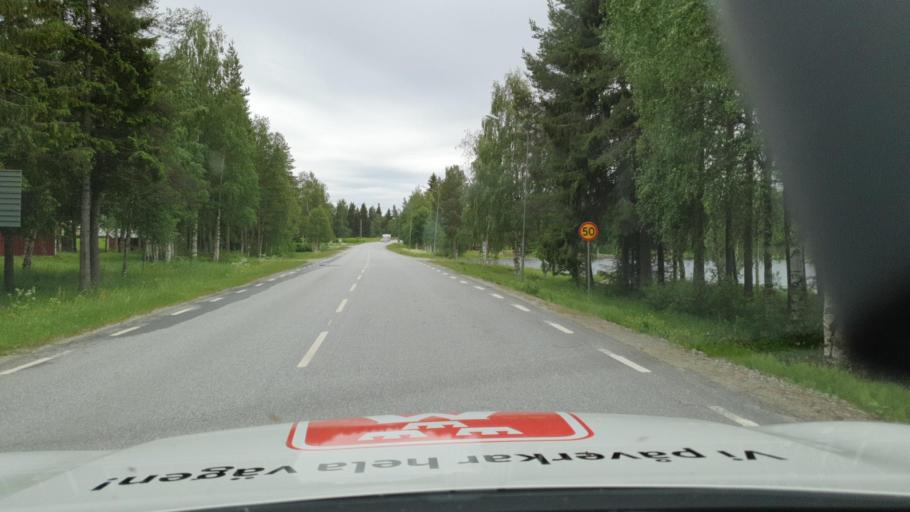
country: SE
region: Vaesterbotten
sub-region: Lycksele Kommun
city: Lycksele
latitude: 64.0764
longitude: 18.3995
